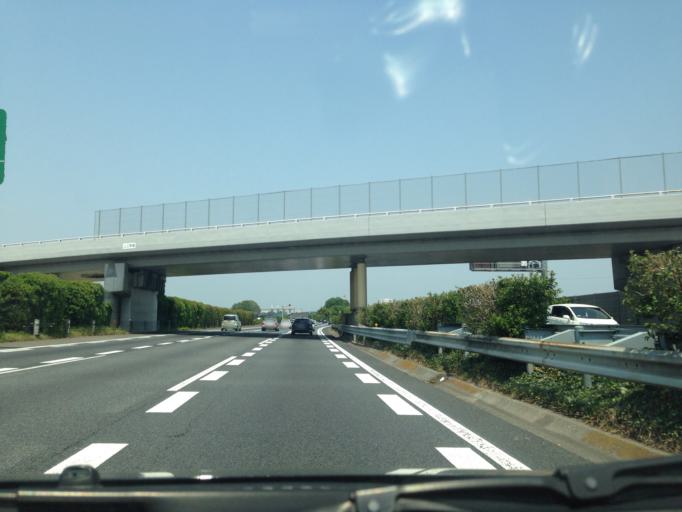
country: JP
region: Gunma
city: Tatebayashi
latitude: 36.2137
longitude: 139.5695
